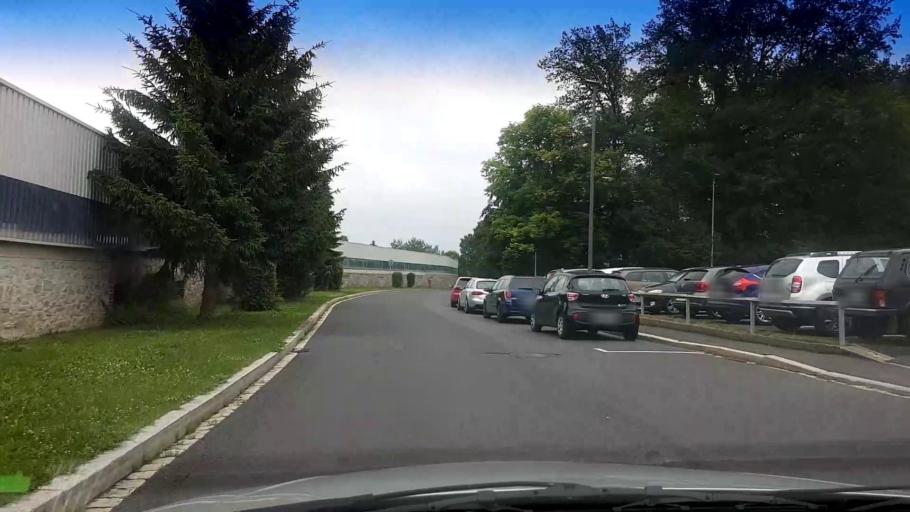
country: DE
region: Bavaria
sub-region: Upper Franconia
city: Marktredwitz
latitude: 50.0100
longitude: 12.0845
